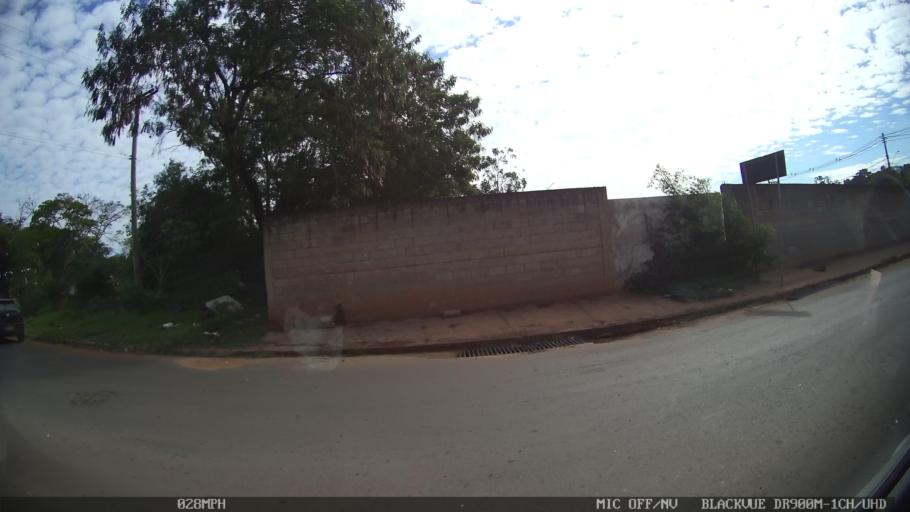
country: BR
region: Sao Paulo
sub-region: Santa Barbara D'Oeste
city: Santa Barbara d'Oeste
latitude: -22.7754
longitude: -47.4037
